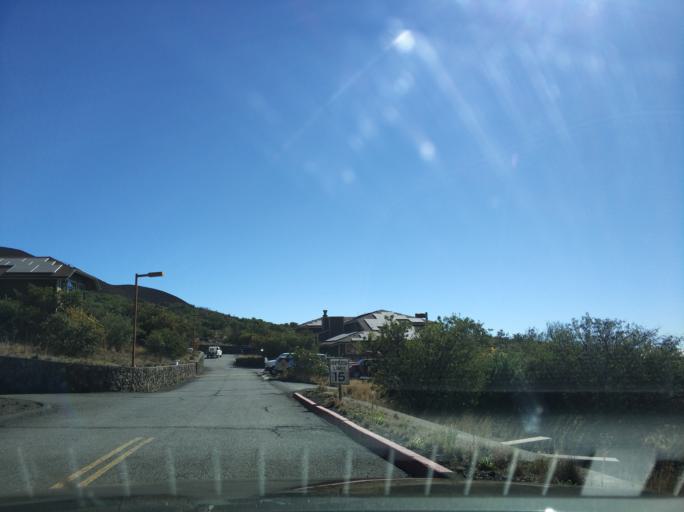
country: US
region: Hawaii
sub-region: Hawaii County
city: Honoka'a
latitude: 19.7616
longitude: -155.4566
